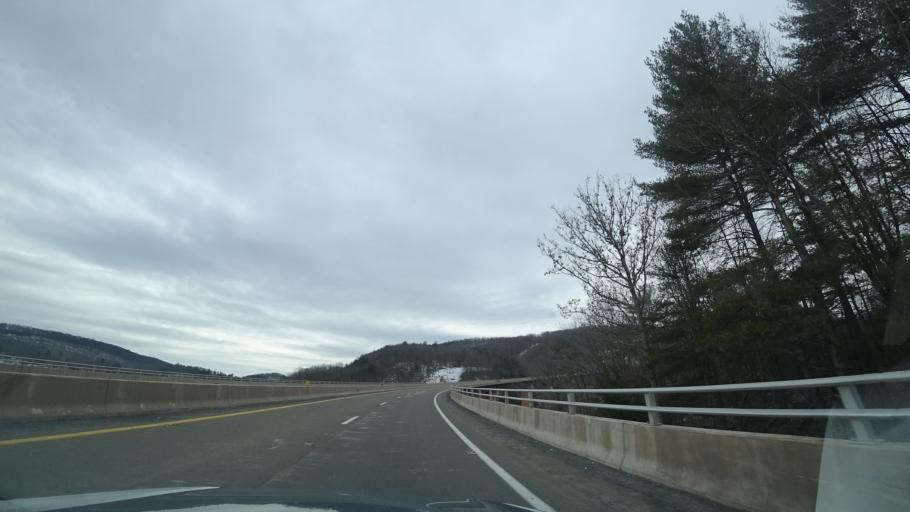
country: US
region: Virginia
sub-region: Shenandoah County
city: Basye
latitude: 39.0430
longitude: -78.7092
